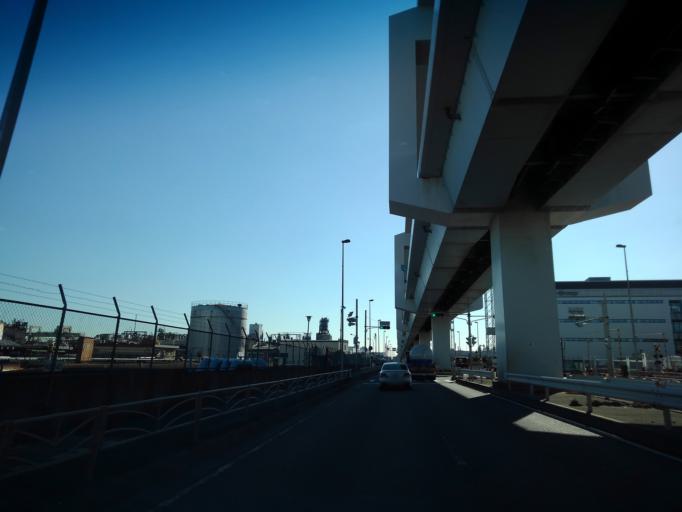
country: JP
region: Kanagawa
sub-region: Kawasaki-shi
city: Kawasaki
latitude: 35.5293
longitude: 139.7731
